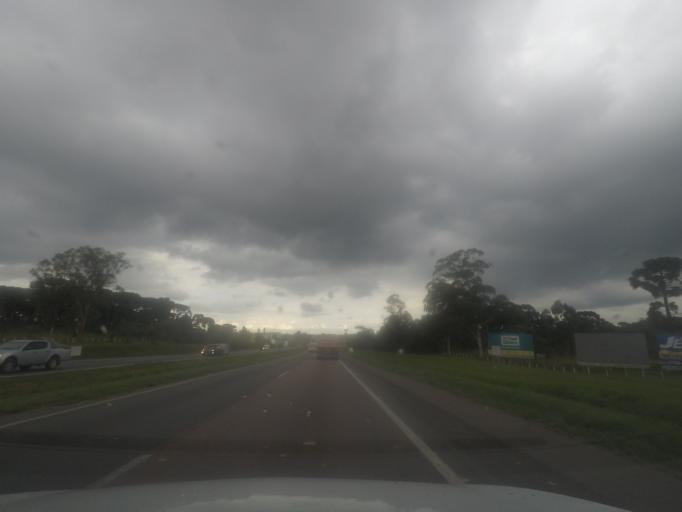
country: BR
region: Parana
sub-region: Sao Jose Dos Pinhais
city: Sao Jose dos Pinhais
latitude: -25.5628
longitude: -49.2580
